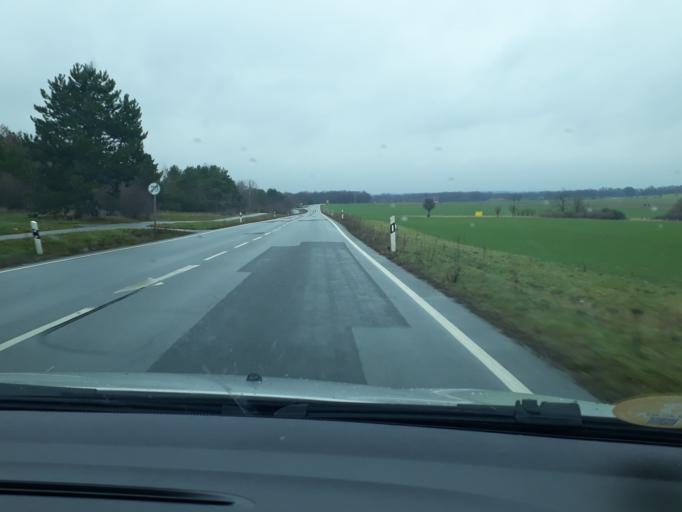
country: DE
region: Saxony
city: Bautzen
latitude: 51.2036
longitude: 14.4688
